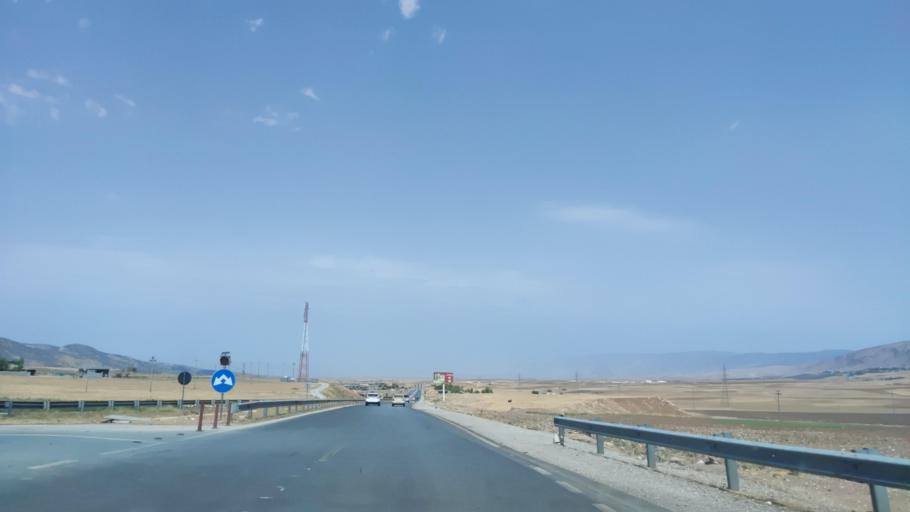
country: IQ
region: Arbil
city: Shaqlawah
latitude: 36.4937
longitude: 44.3689
